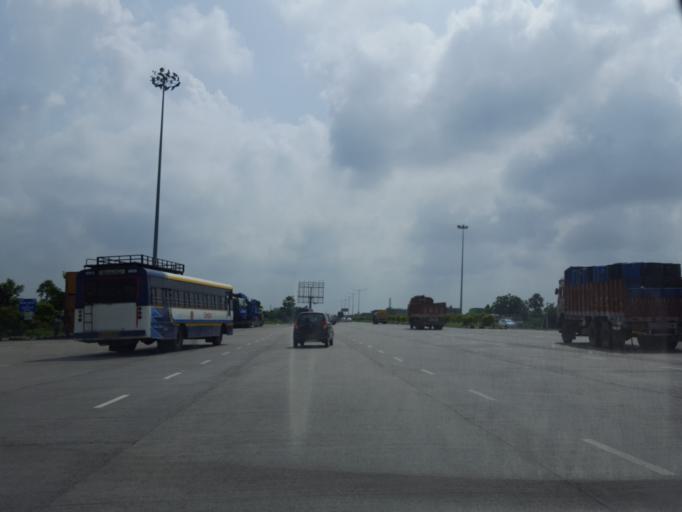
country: IN
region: Telangana
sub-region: Nalgonda
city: Bhongir
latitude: 17.2329
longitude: 78.9614
